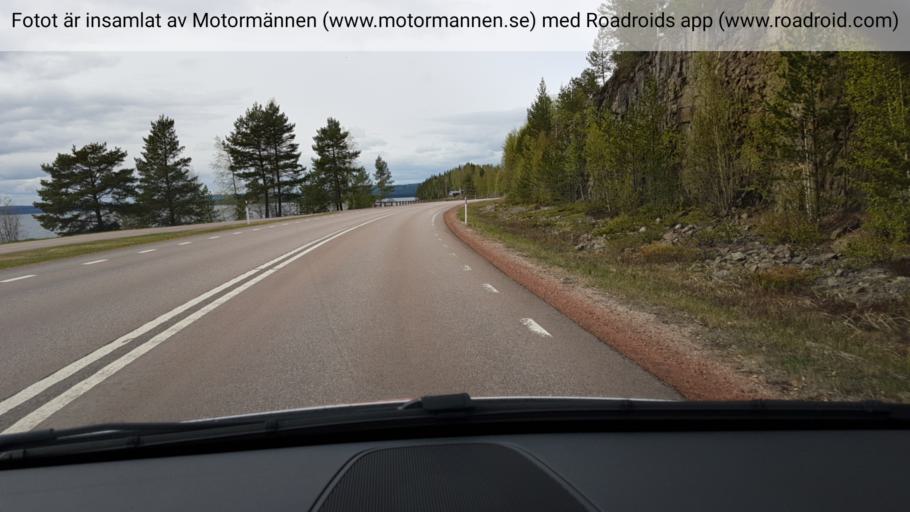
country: SE
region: Jaemtland
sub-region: Ragunda Kommun
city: Hammarstrand
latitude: 63.1415
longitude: 16.0061
